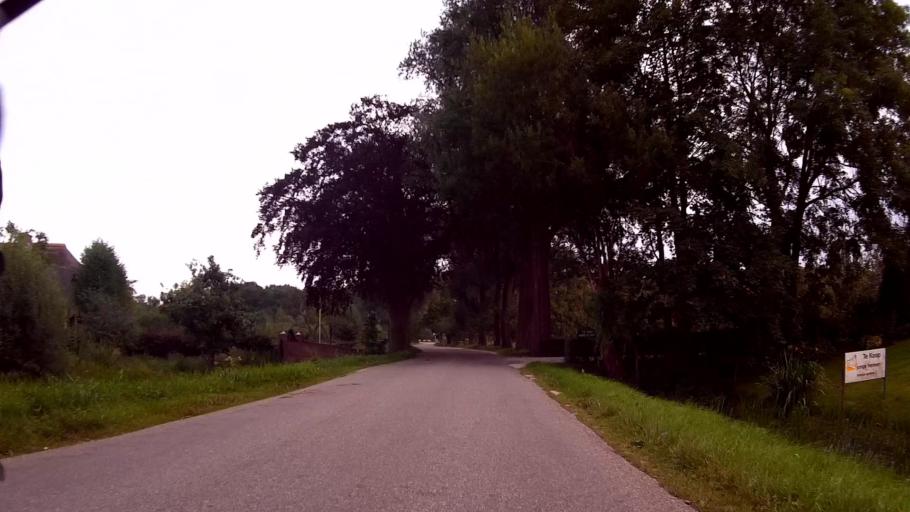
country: NL
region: Utrecht
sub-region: Gemeente De Bilt
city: De Bilt
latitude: 52.1112
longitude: 5.1541
